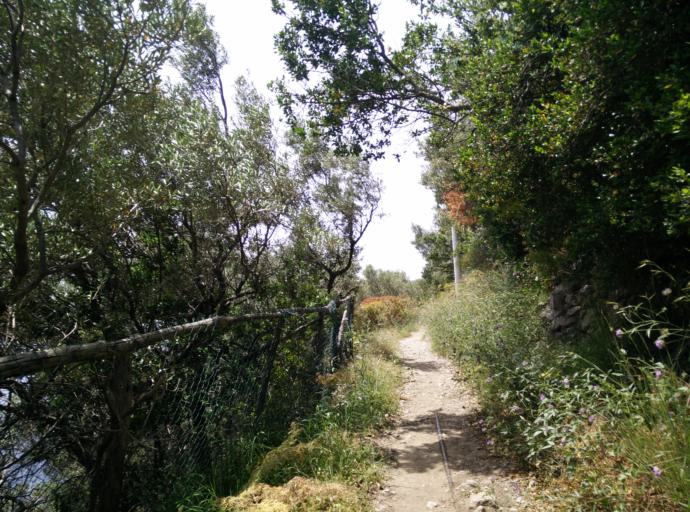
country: IT
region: Campania
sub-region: Provincia di Napoli
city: Massa Lubrense
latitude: 40.5825
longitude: 14.3481
